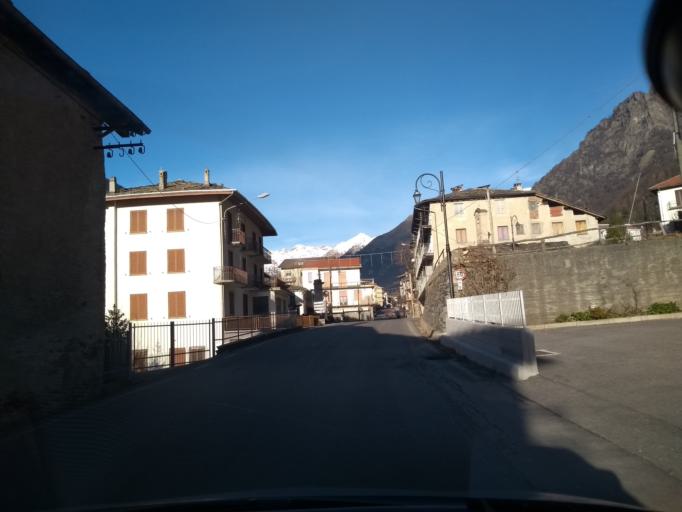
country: IT
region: Piedmont
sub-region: Provincia di Torino
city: Cantoira
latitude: 45.3411
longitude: 7.3832
